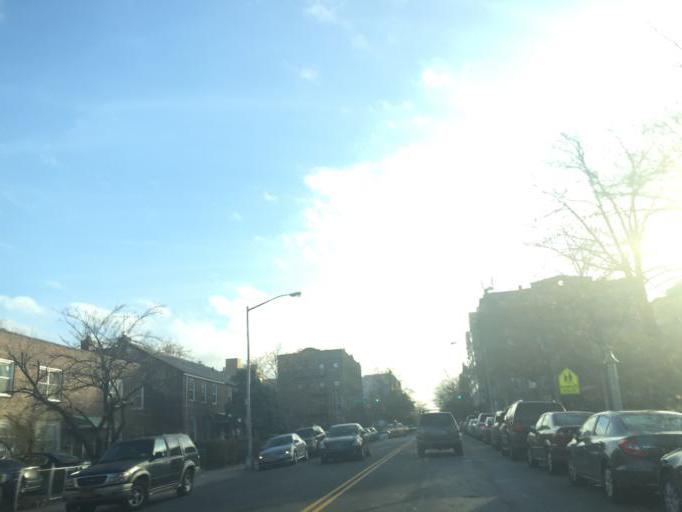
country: US
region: New York
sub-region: Queens County
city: Long Island City
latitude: 40.7477
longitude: -73.9207
